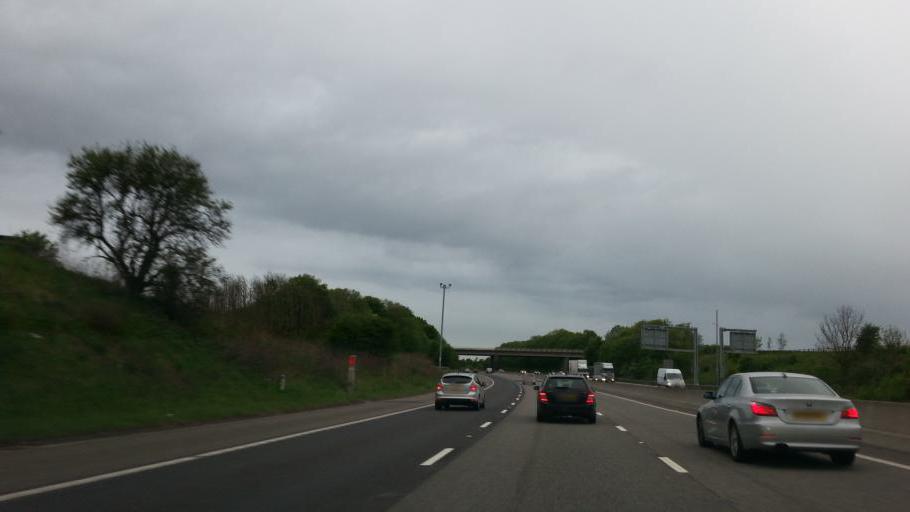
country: GB
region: England
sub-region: Rotherham
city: Ulley
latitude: 53.3952
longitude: -1.2877
